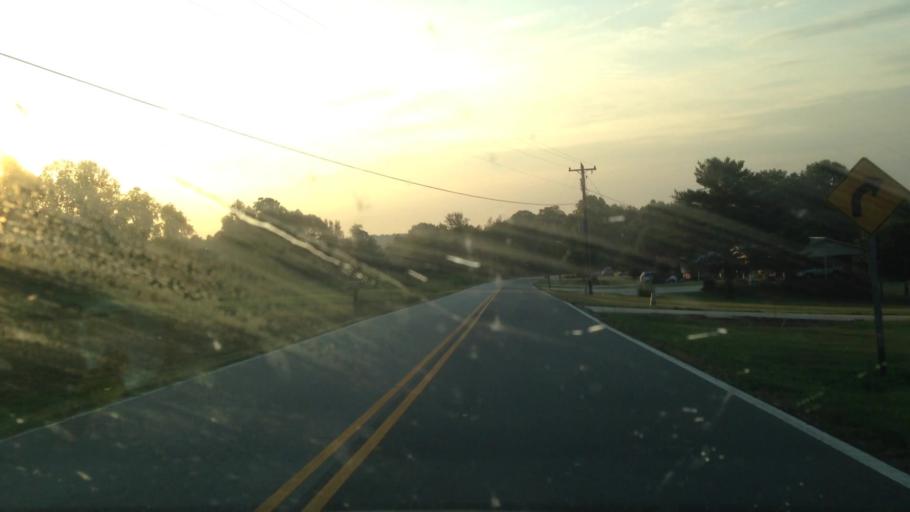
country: US
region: North Carolina
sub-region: Forsyth County
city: Walkertown
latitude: 36.1591
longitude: -80.1144
